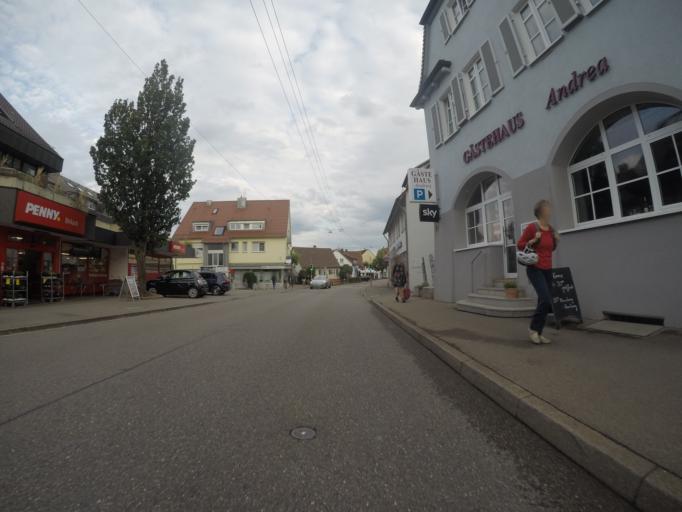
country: DE
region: Baden-Wuerttemberg
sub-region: Regierungsbezirk Stuttgart
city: Ostfildern
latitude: 48.7225
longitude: 9.2085
